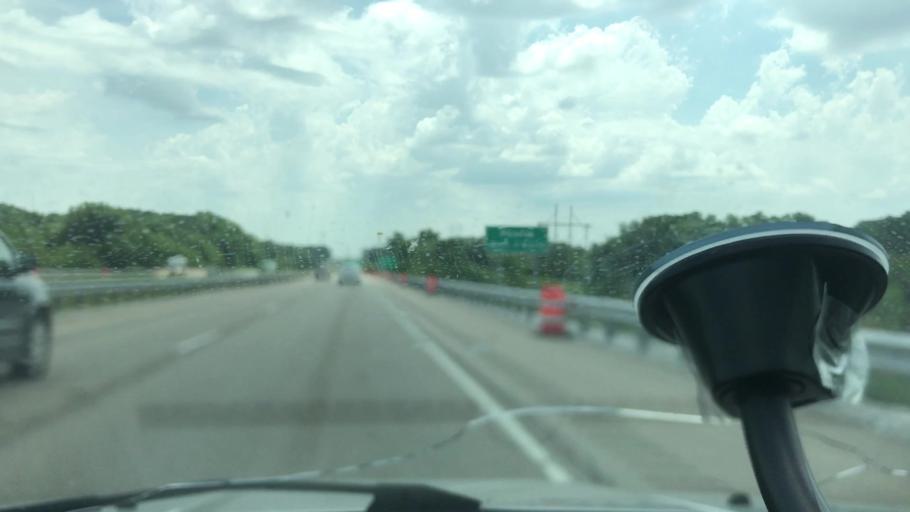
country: US
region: Illinois
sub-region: Peoria County
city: West Peoria
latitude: 40.7403
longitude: -89.6570
